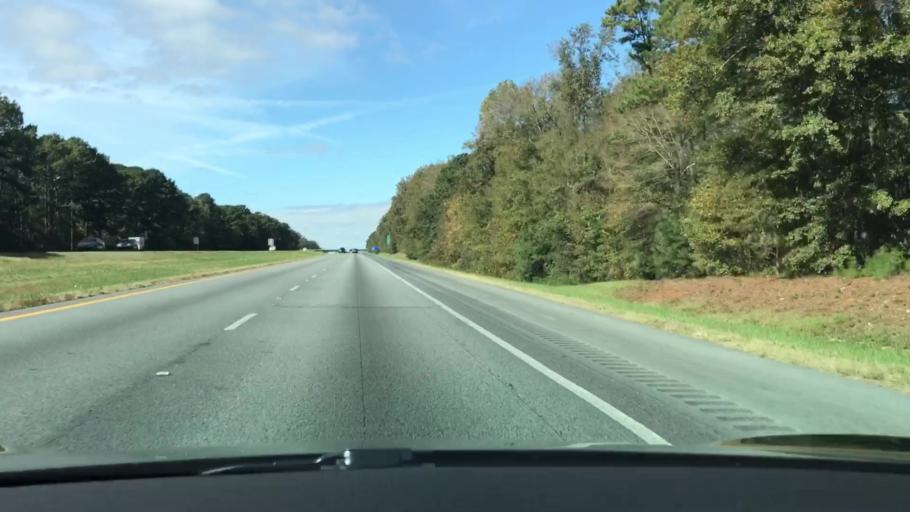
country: US
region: Georgia
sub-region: Morgan County
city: Madison
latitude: 33.5848
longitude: -83.6019
